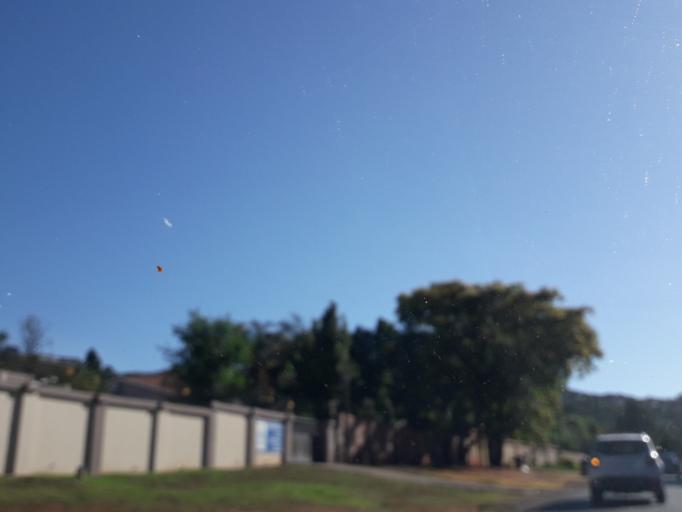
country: ZA
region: Gauteng
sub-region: City of Johannesburg Metropolitan Municipality
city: Roodepoort
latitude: -26.1493
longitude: 27.9497
